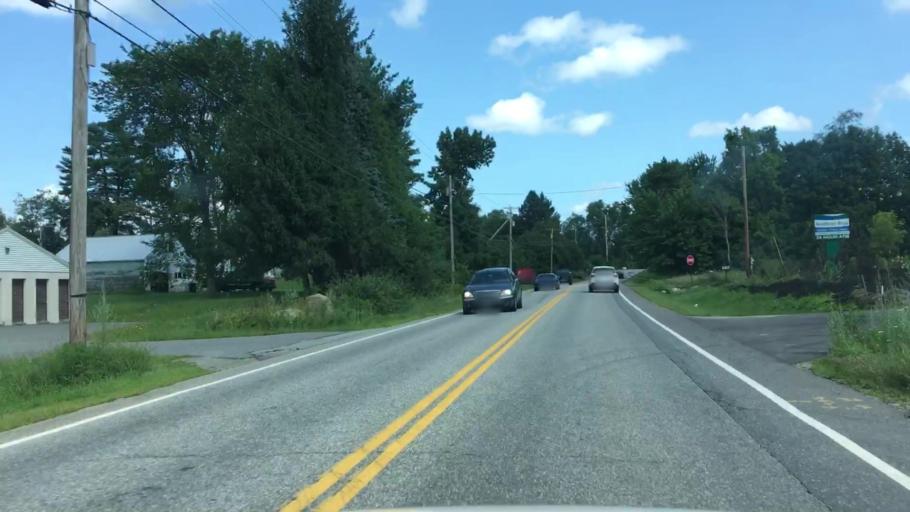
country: US
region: Maine
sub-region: Kennebec County
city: Augusta
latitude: 44.3285
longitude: -69.8177
